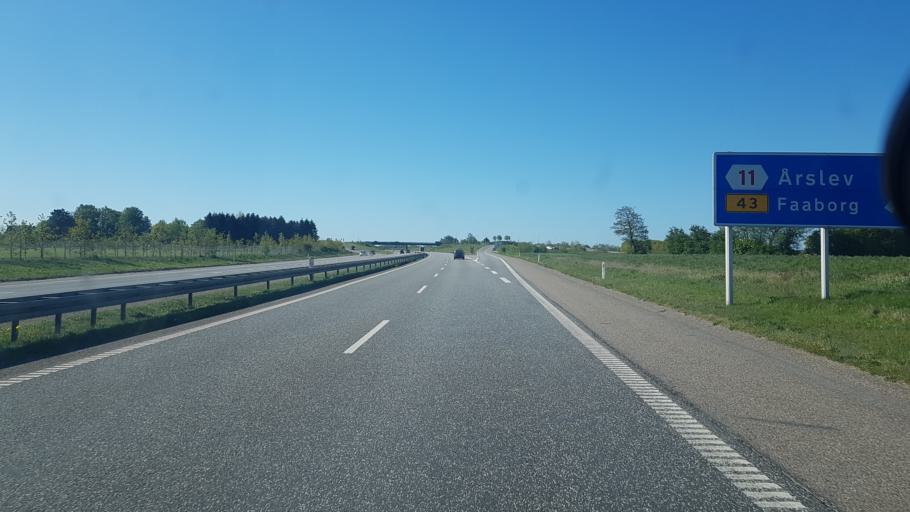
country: DK
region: South Denmark
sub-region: Faaborg-Midtfyn Kommune
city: Arslev
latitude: 55.3104
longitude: 10.4367
